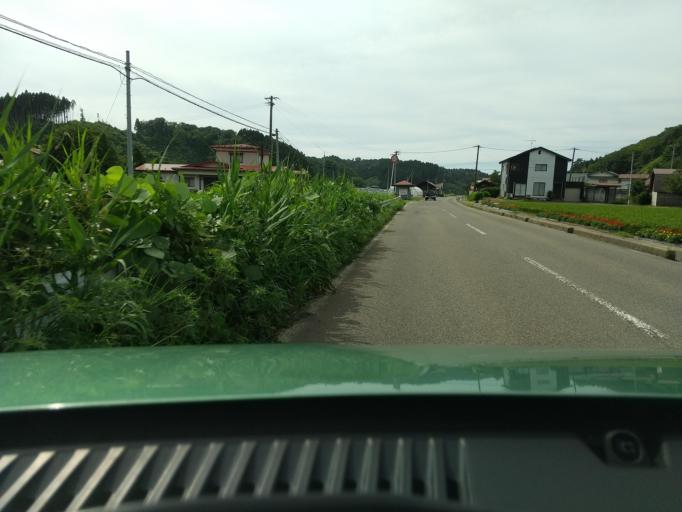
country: JP
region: Akita
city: Akita
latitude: 39.7820
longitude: 140.1309
